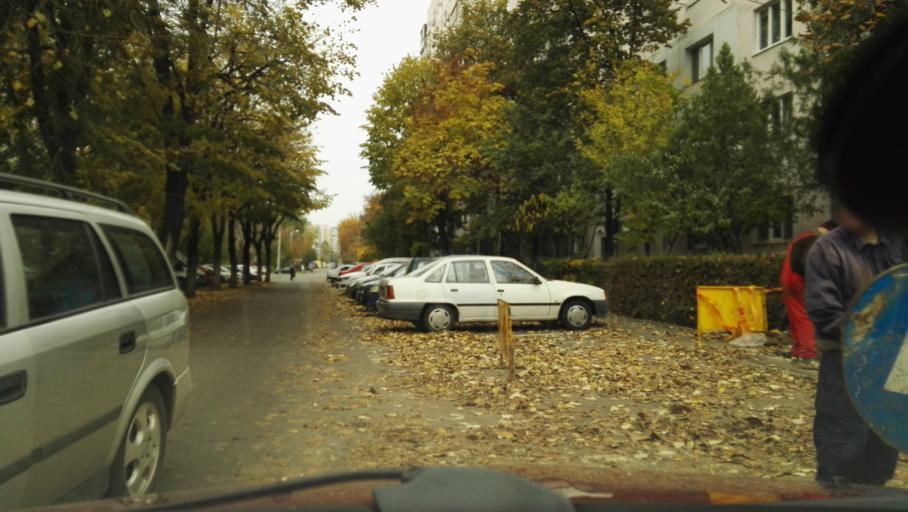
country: RO
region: Bucuresti
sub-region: Municipiul Bucuresti
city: Bucuresti
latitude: 44.3908
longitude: 26.1128
